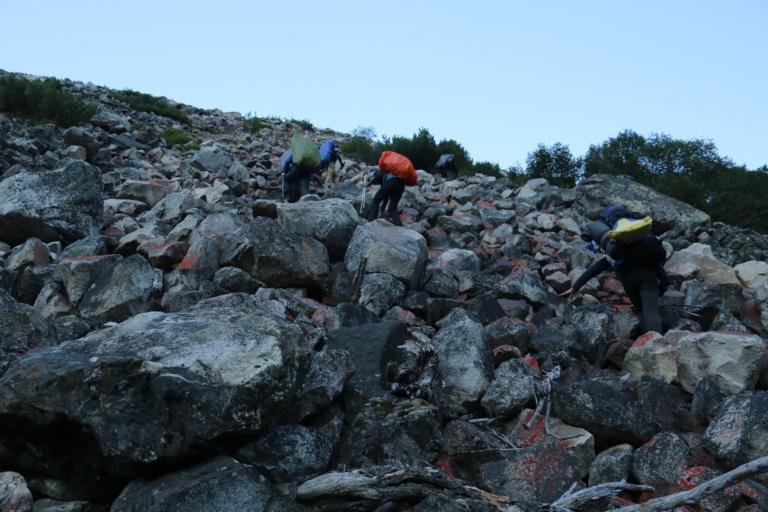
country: RU
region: Respublika Buryatiya
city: Novyy Uoyan
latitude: 56.3250
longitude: 111.1939
